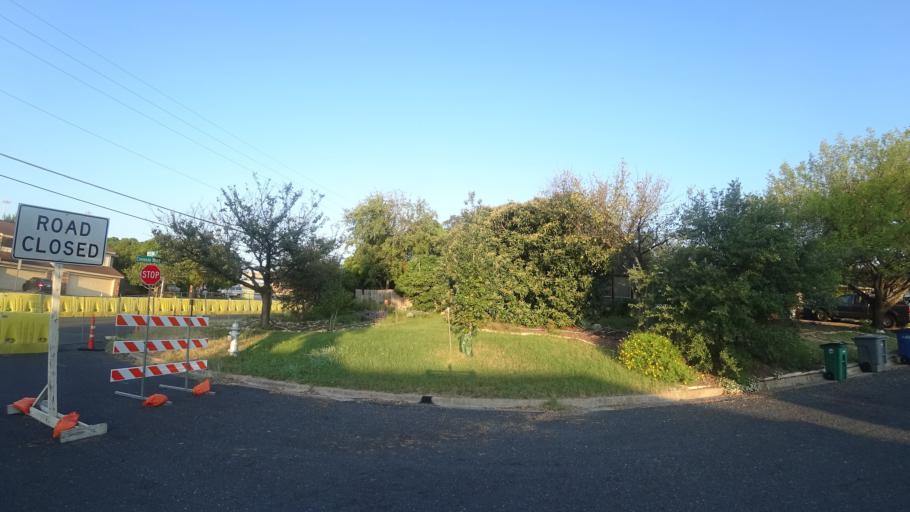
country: US
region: Texas
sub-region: Travis County
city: Austin
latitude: 30.3263
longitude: -97.6857
